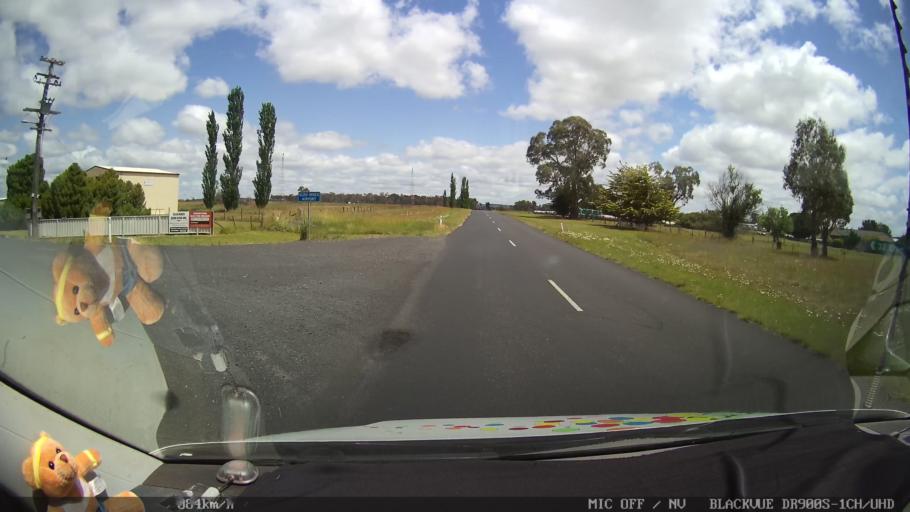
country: AU
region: New South Wales
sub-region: Glen Innes Severn
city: Glen Innes
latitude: -29.6740
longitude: 151.6962
